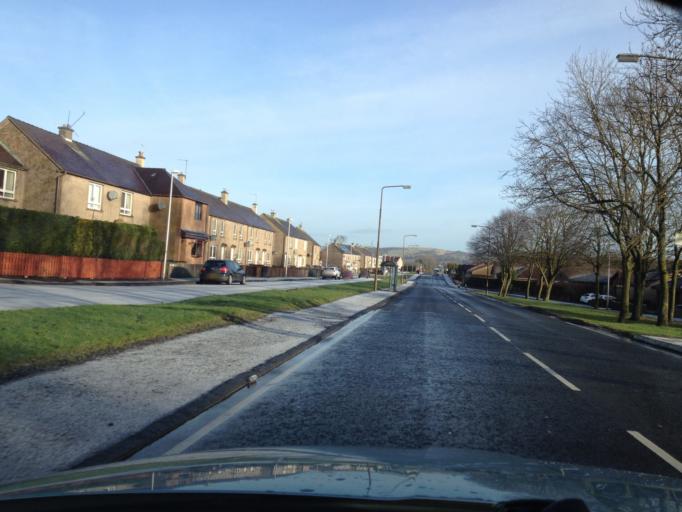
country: GB
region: Scotland
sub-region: West Lothian
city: Bathgate
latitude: 55.8886
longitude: -3.6555
